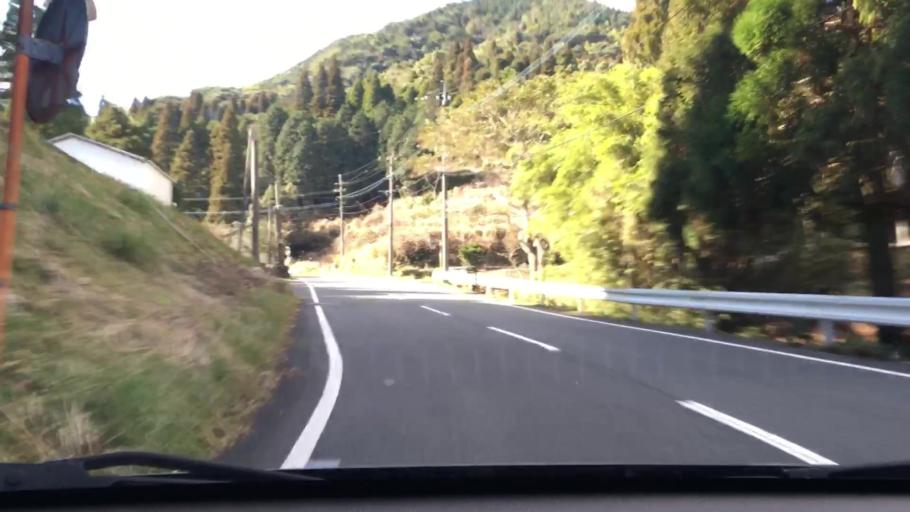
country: JP
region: Kagoshima
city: Ijuin
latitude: 31.7178
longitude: 130.4292
